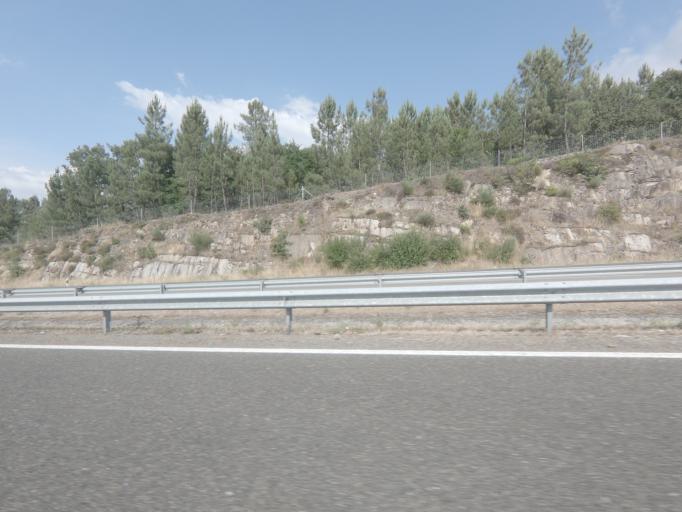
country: ES
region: Galicia
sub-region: Provincia de Ourense
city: Taboadela
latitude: 42.2708
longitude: -7.8716
